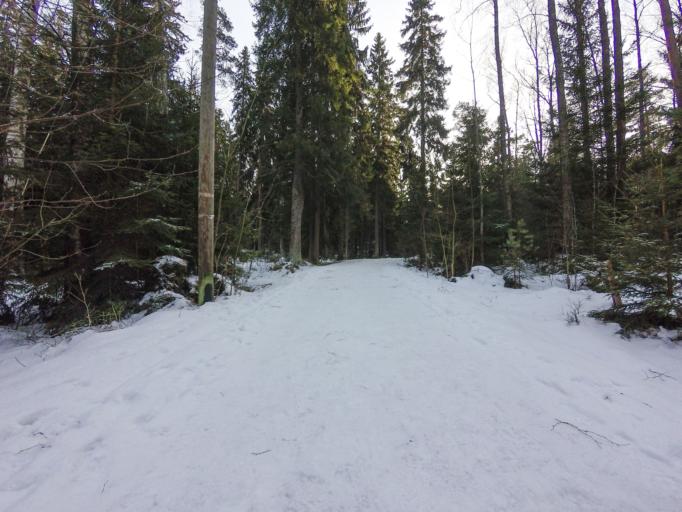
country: FI
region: Uusimaa
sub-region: Helsinki
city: Helsinki
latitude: 60.1760
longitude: 25.0281
